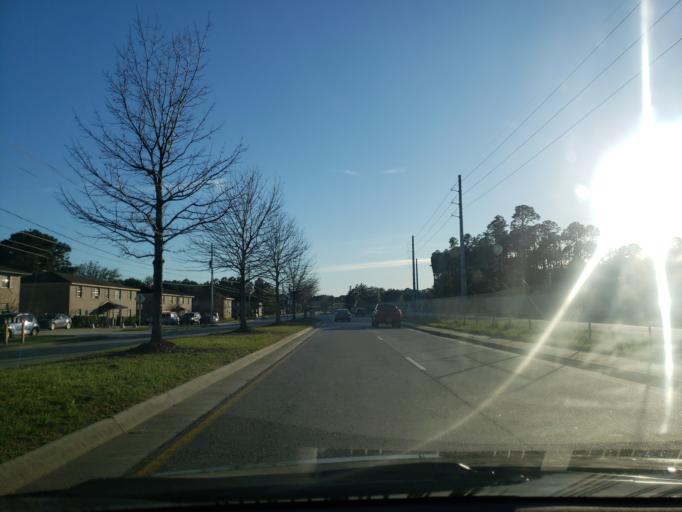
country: US
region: Georgia
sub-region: Chatham County
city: Montgomery
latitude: 32.0019
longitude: -81.1438
